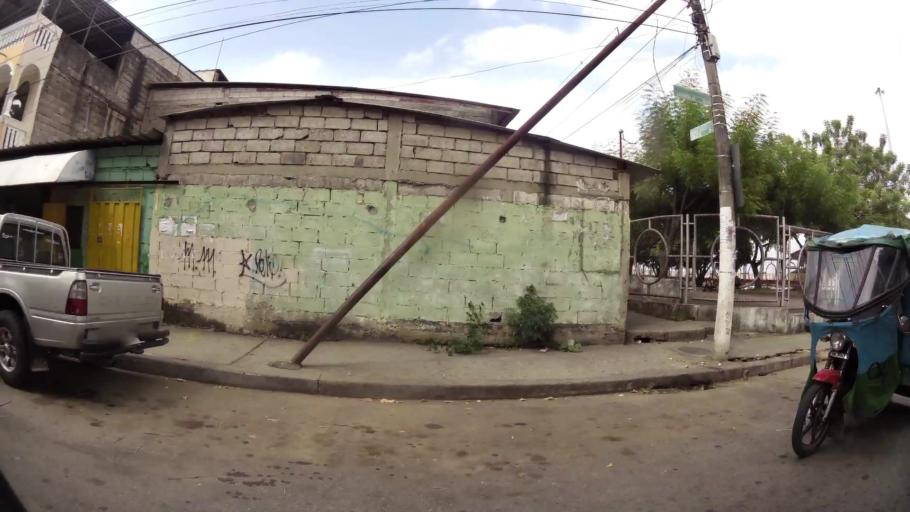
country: EC
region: Guayas
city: Santa Lucia
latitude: -2.0914
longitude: -79.9410
